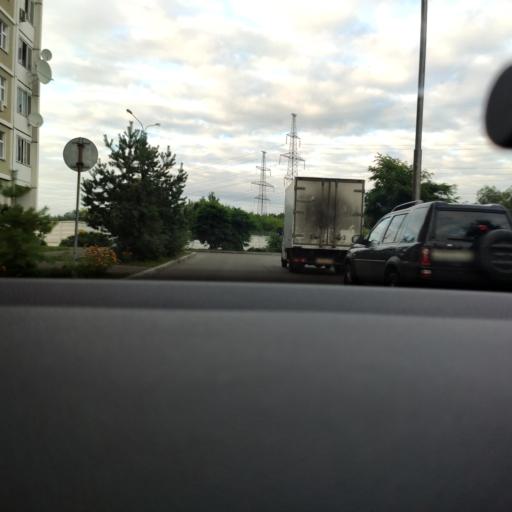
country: RU
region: Moscow
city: Kuz'minki
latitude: 55.6787
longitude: 37.8008
